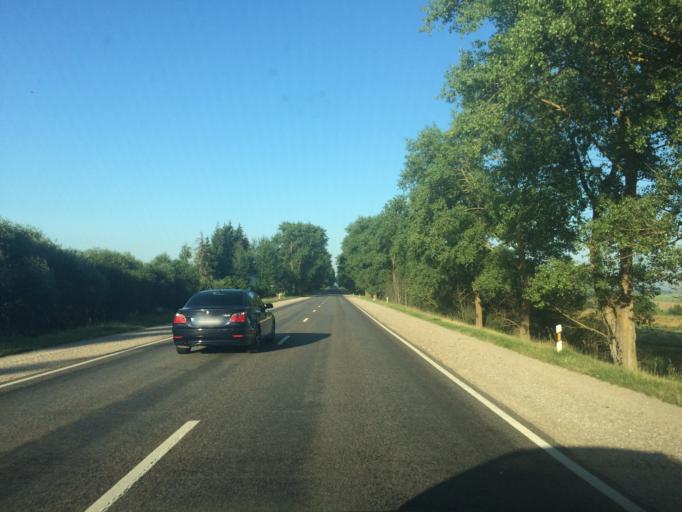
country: LT
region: Utenos apskritis
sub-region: Anyksciai
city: Anyksciai
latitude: 55.3757
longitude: 25.0237
